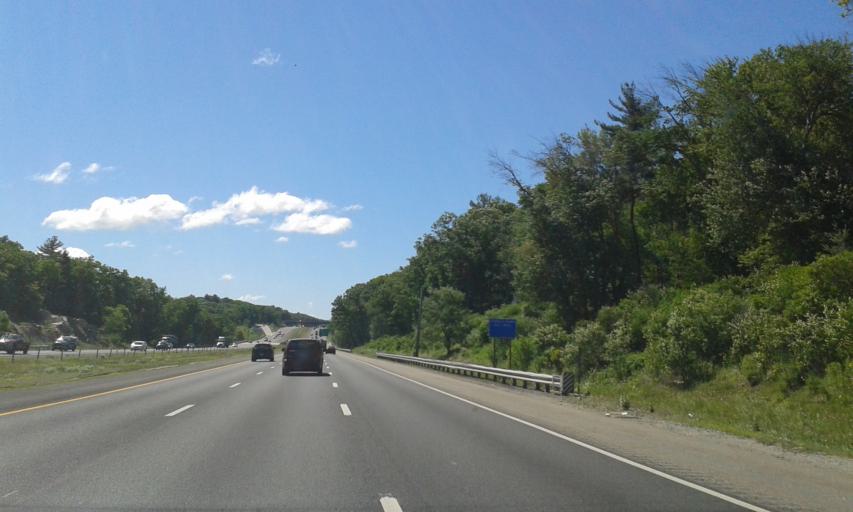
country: US
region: Massachusetts
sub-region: Middlesex County
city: Billerica
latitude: 42.5523
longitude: -71.2913
